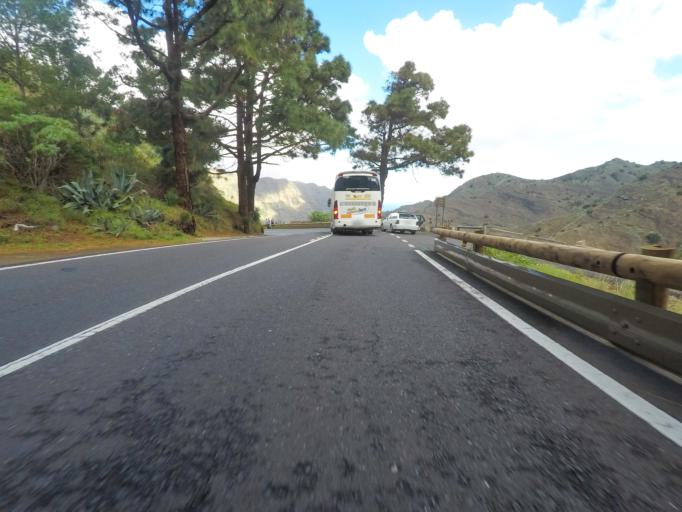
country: ES
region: Canary Islands
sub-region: Provincia de Santa Cruz de Tenerife
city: Hermigua
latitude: 28.1421
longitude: -17.1976
